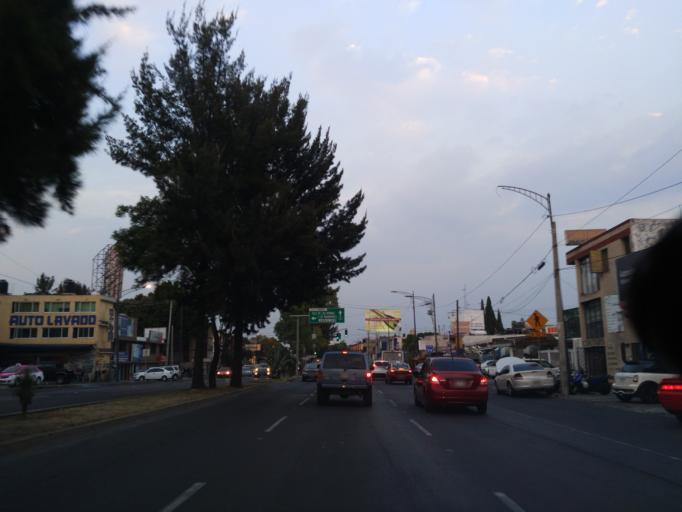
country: MX
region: Mexico City
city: Xochimilco
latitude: 19.3051
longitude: -99.1122
